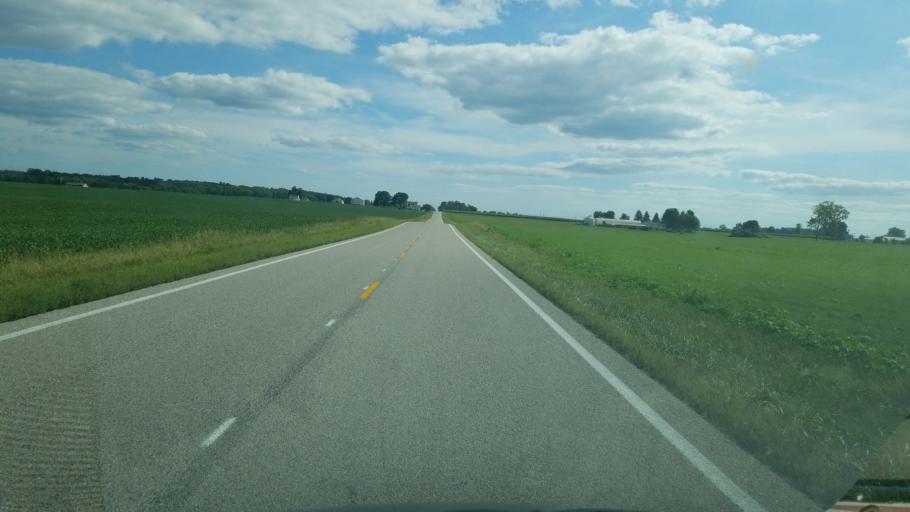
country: US
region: Ohio
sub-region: Logan County
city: De Graff
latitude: 40.2246
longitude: -83.9404
